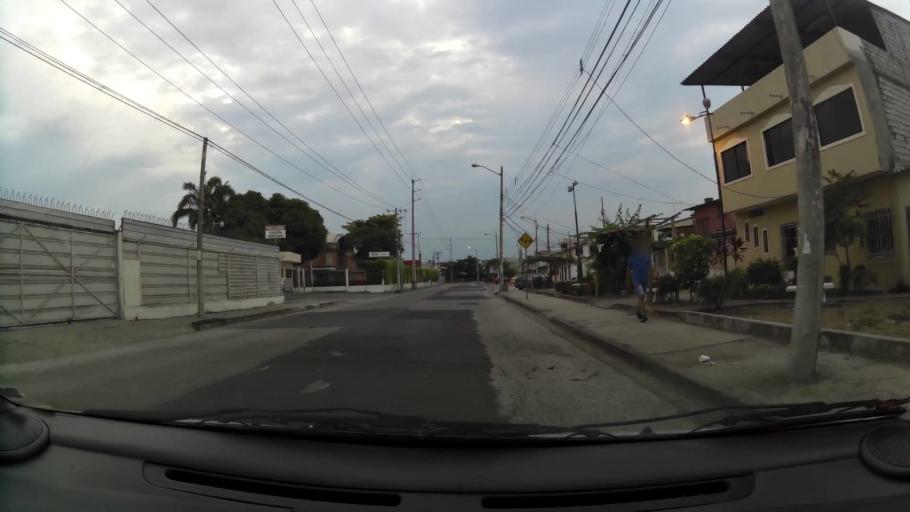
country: EC
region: Guayas
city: Guayaquil
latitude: -2.2414
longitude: -79.8900
